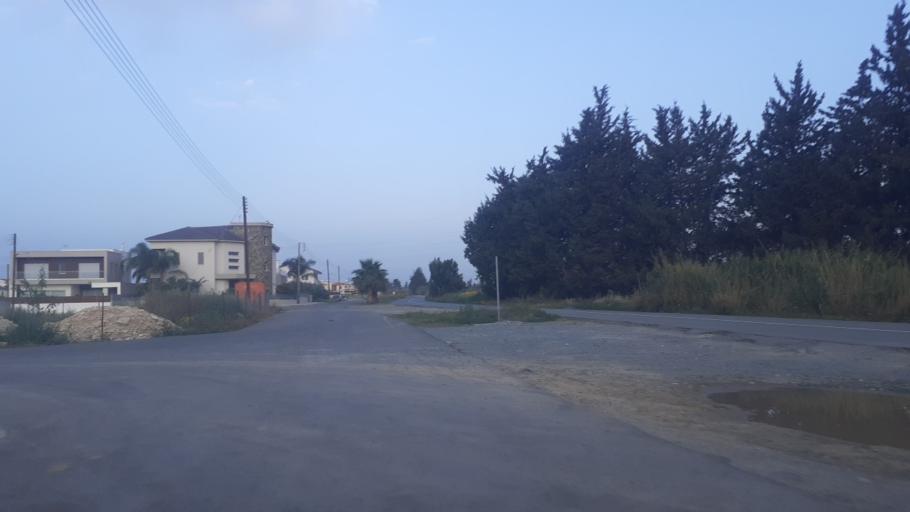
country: CY
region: Limassol
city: Ypsonas
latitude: 34.6626
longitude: 32.9609
